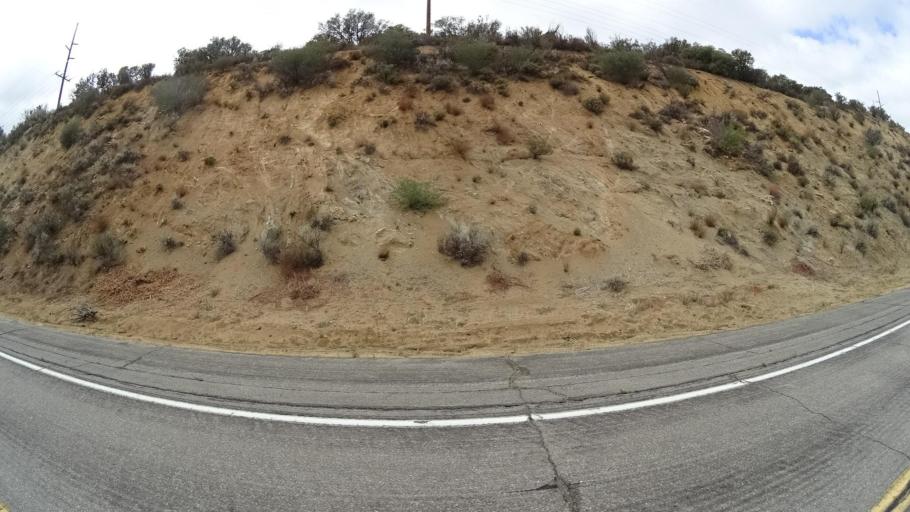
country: US
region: California
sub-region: San Diego County
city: Pine Valley
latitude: 32.7209
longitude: -116.4759
